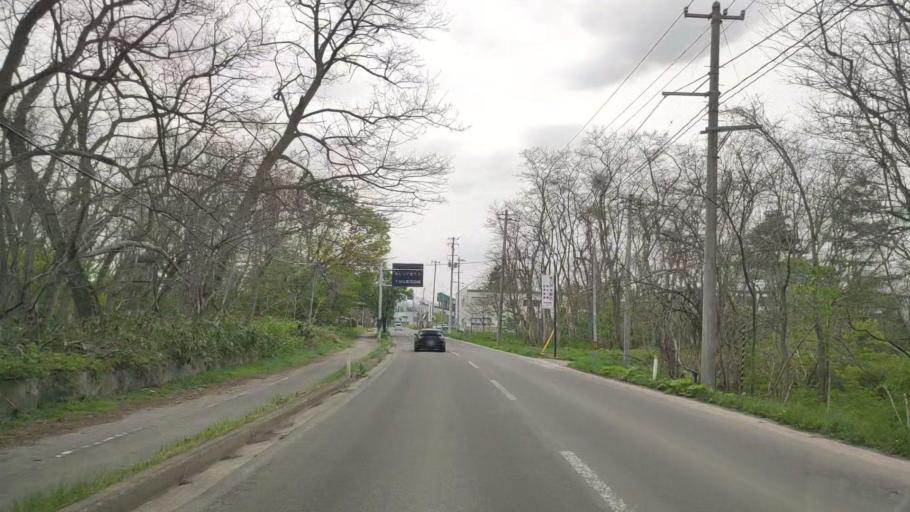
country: JP
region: Aomori
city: Aomori Shi
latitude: 40.7761
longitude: 140.7950
